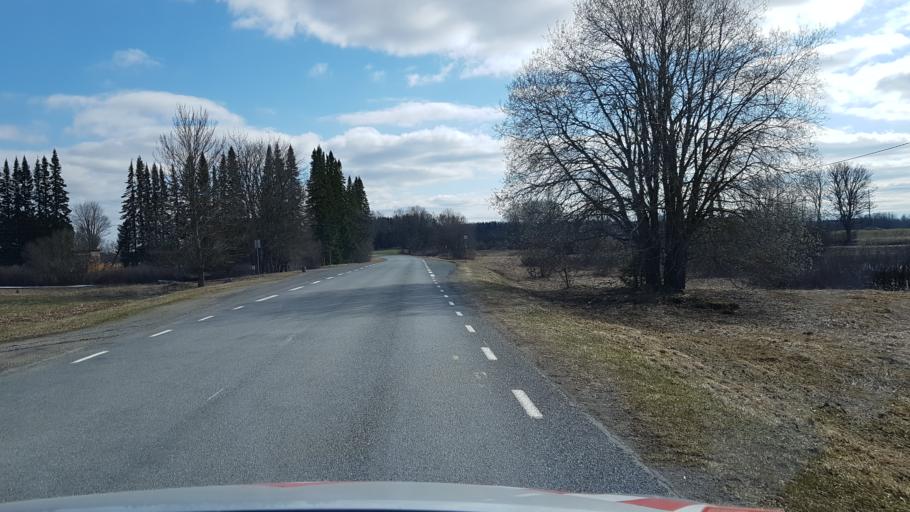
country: EE
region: Laeaene-Virumaa
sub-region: Tamsalu vald
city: Tamsalu
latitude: 59.1774
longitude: 26.0528
